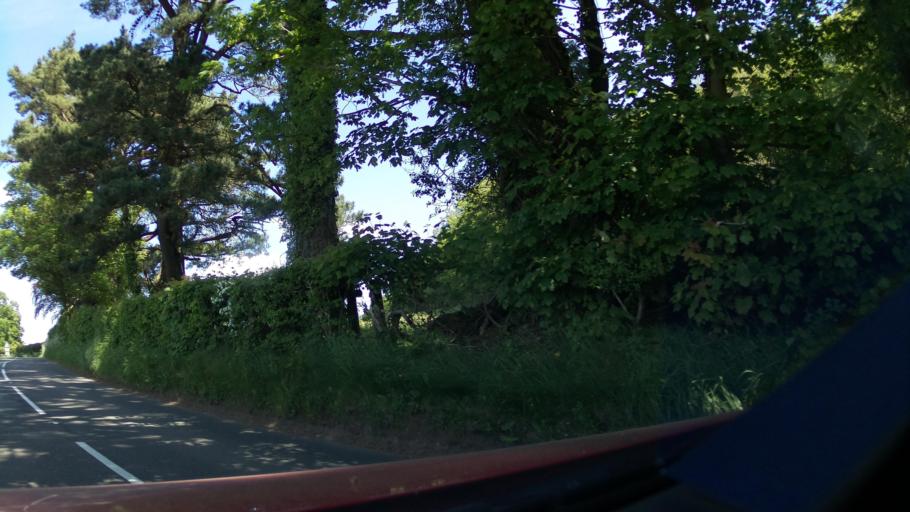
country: GB
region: Wales
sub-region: Monmouthshire
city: Tintern
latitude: 51.6817
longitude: -2.7520
